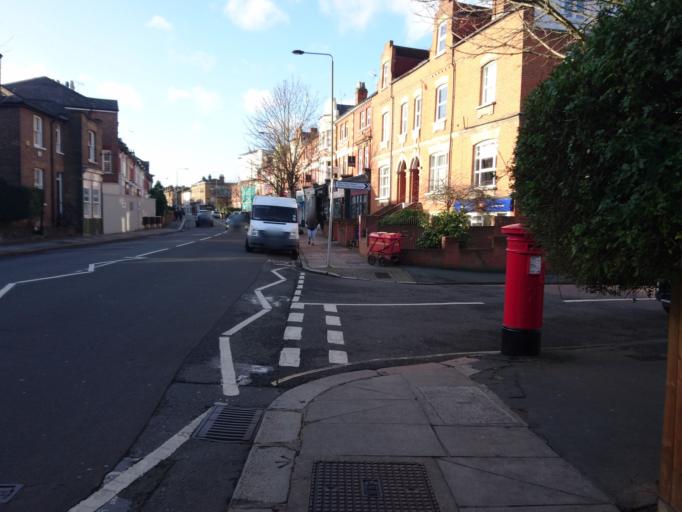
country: GB
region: England
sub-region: Greater London
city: Richmond
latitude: 51.4622
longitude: -0.2937
